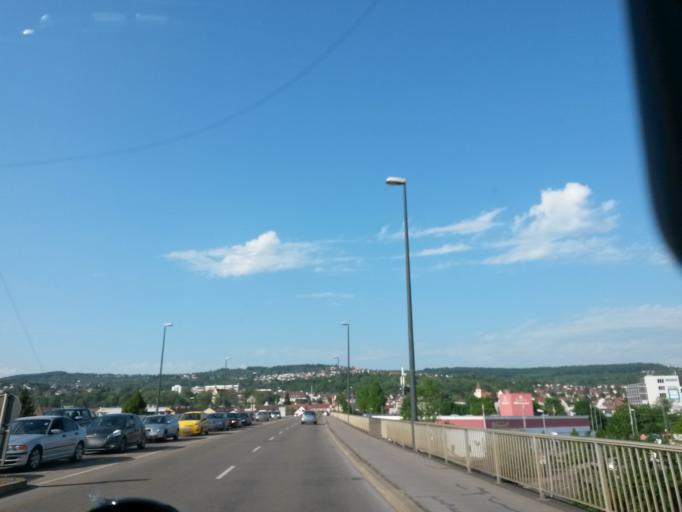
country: DE
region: Baden-Wuerttemberg
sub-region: Regierungsbezirk Stuttgart
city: Esslingen
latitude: 48.7298
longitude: 9.3215
